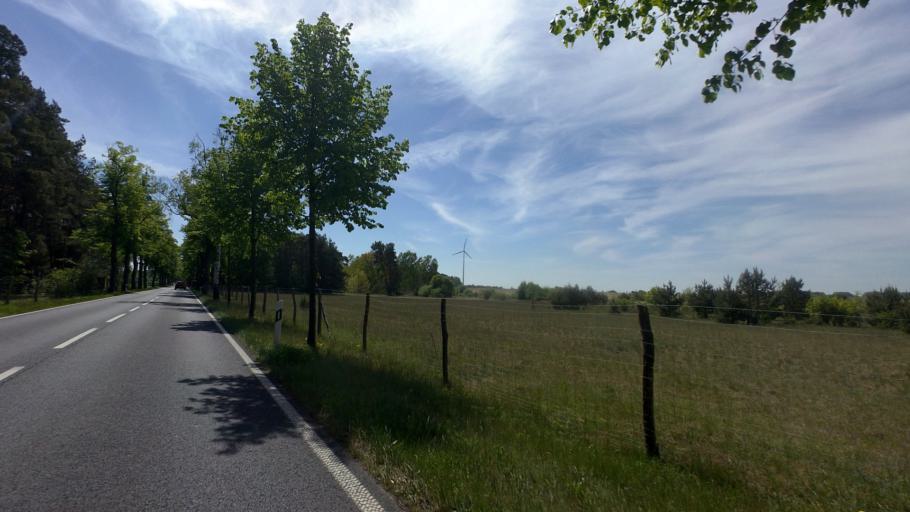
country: DE
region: Brandenburg
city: Luckenwalde
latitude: 52.1214
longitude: 13.1342
